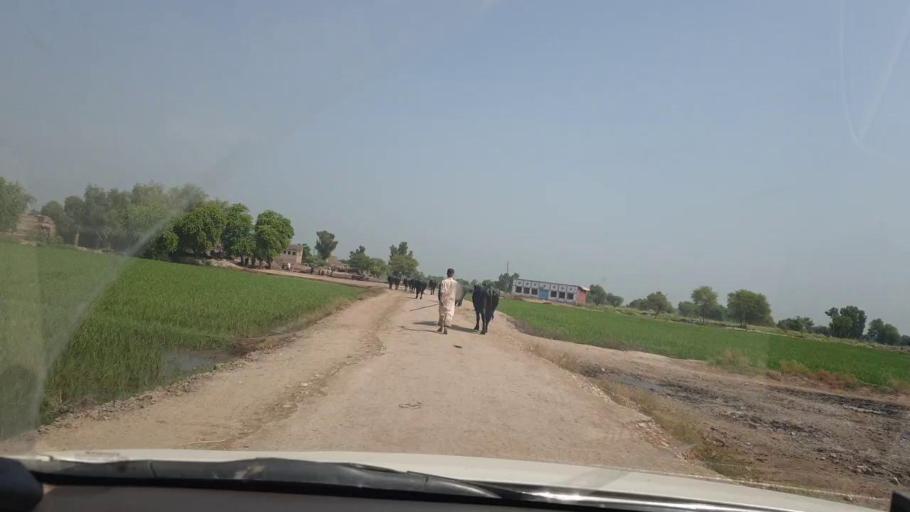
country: PK
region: Sindh
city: Chak
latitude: 27.8798
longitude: 68.7819
